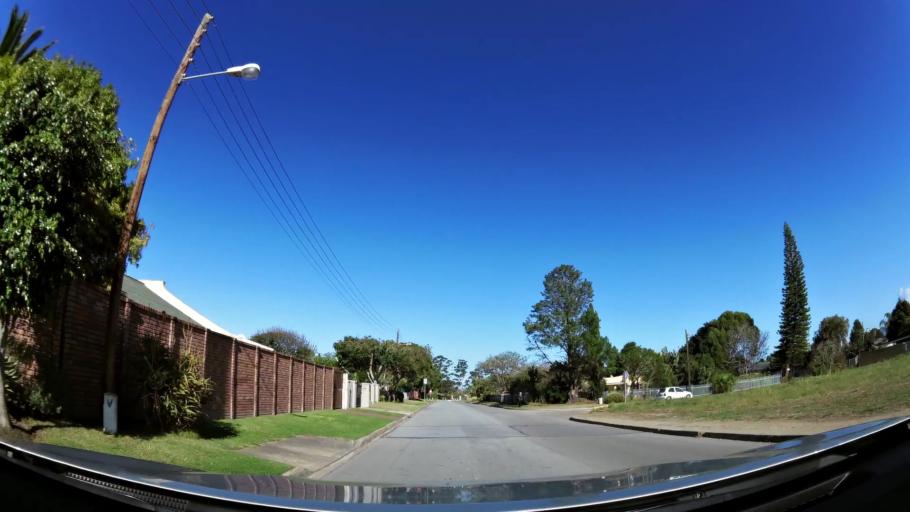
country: ZA
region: Western Cape
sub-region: Eden District Municipality
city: George
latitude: -33.9486
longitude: 22.4157
